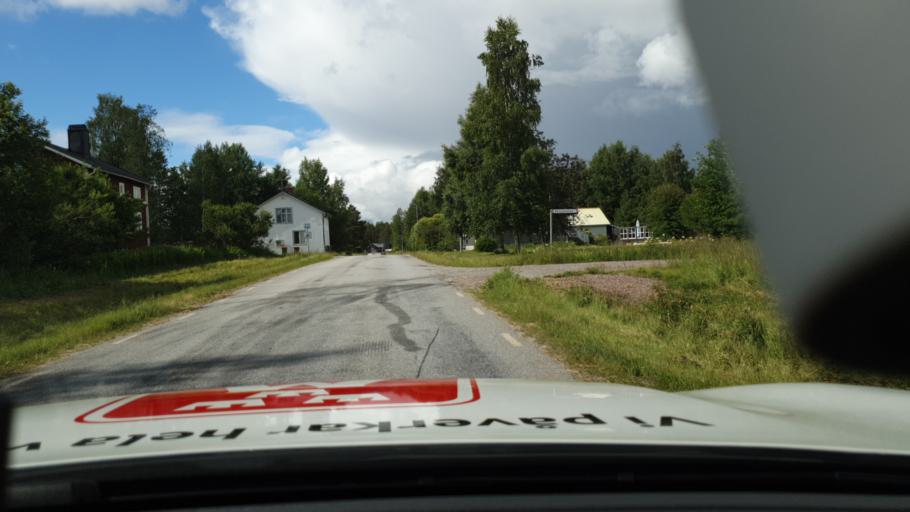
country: SE
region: Norrbotten
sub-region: Pitea Kommun
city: Rosvik
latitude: 65.3917
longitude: 21.7355
